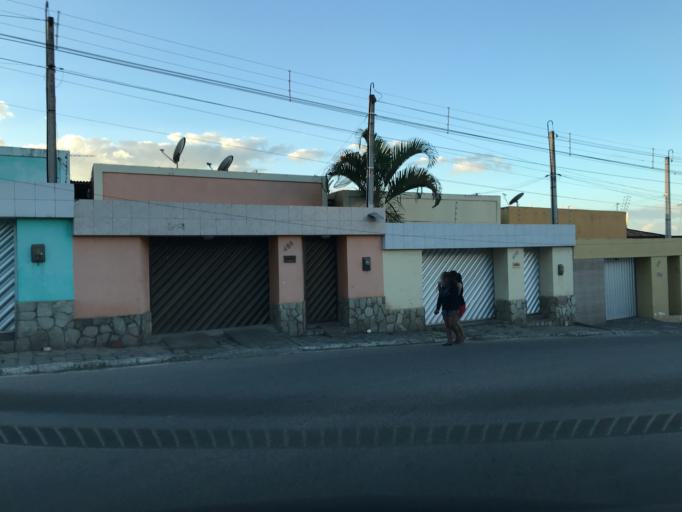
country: BR
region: Pernambuco
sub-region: Bezerros
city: Bezerros
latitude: -8.2385
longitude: -35.7609
